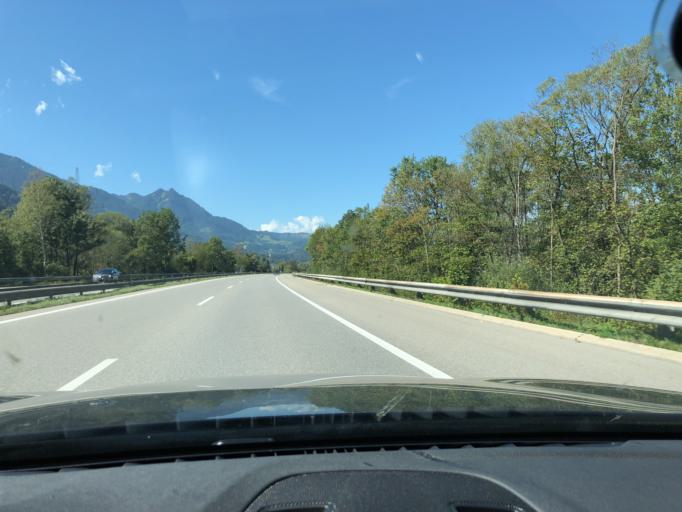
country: AT
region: Vorarlberg
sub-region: Politischer Bezirk Bludenz
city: Bludesch
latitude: 47.1766
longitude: 9.7404
